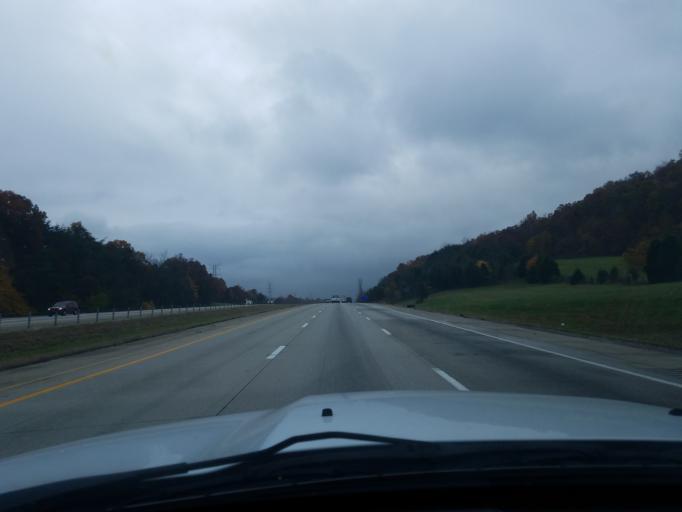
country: US
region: Kentucky
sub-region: Bullitt County
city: Lebanon Junction
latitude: 37.8403
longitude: -85.7166
